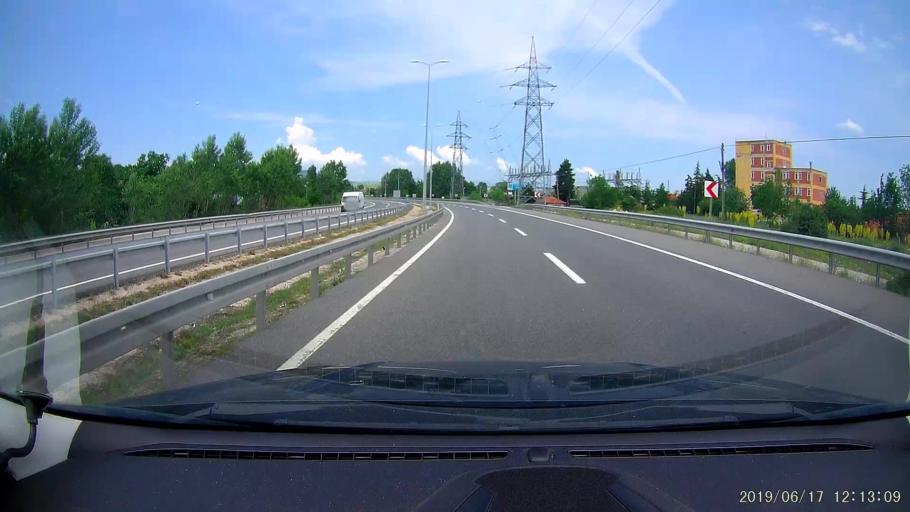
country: TR
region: Karabuk
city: Gozyeri
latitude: 40.8681
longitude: 32.6332
